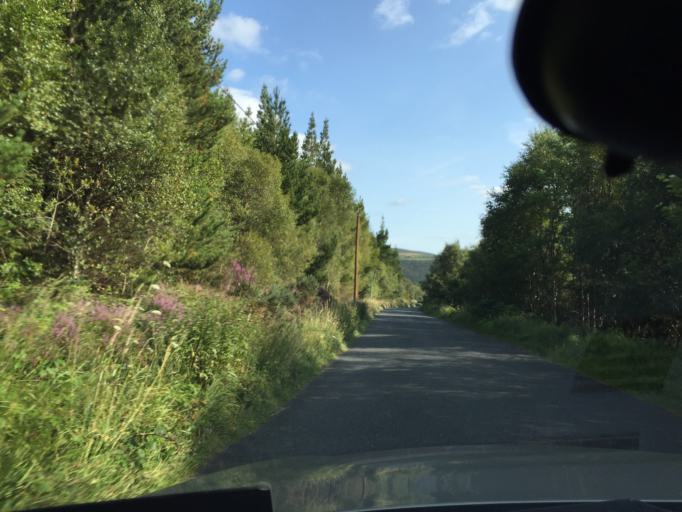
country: IE
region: Leinster
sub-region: Wicklow
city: Rathdrum
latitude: 53.0156
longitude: -6.3005
